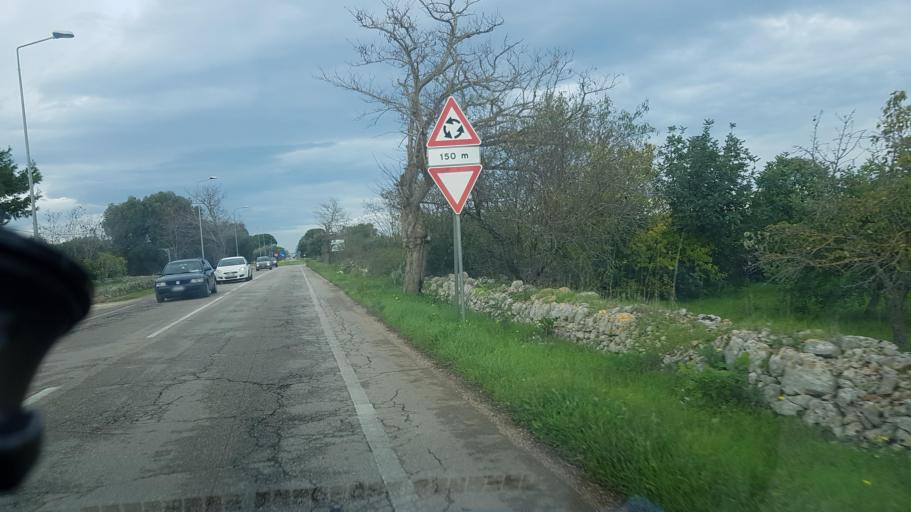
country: IT
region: Apulia
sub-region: Provincia di Brindisi
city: San Vito dei Normanni
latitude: 40.6681
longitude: 17.6967
